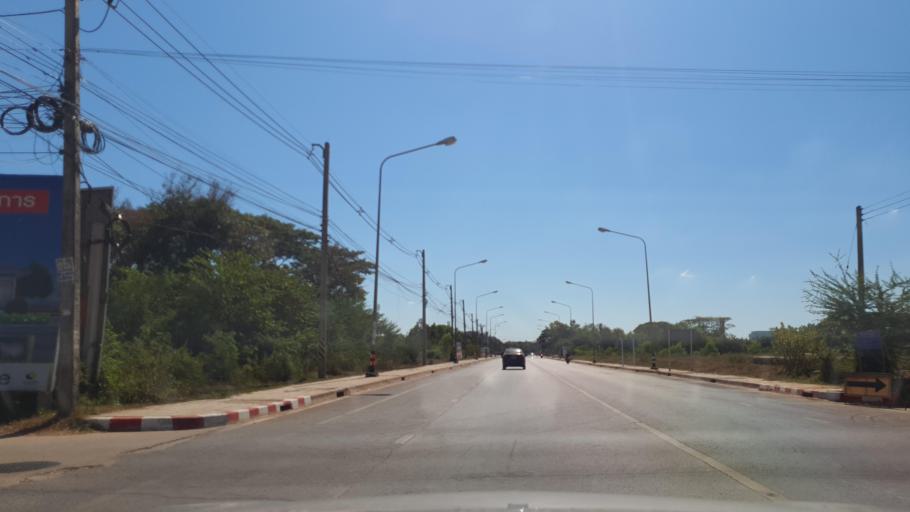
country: TH
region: Sakon Nakhon
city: Sakon Nakhon
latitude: 17.1515
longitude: 104.1285
